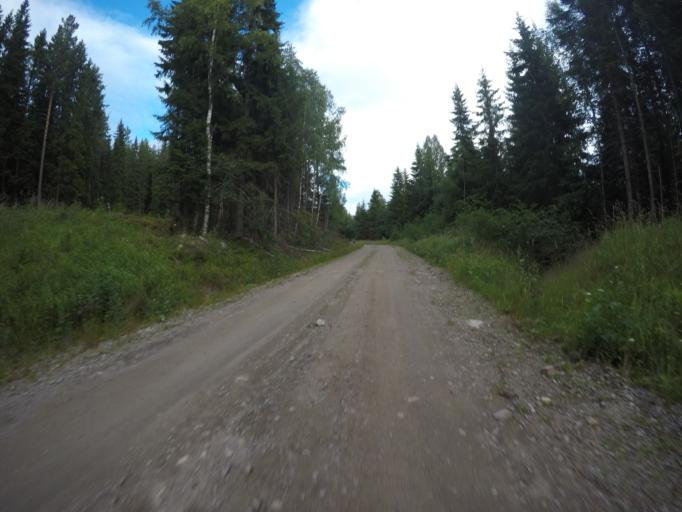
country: SE
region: Vaermland
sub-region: Filipstads Kommun
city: Lesjofors
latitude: 60.0104
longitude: 14.4208
